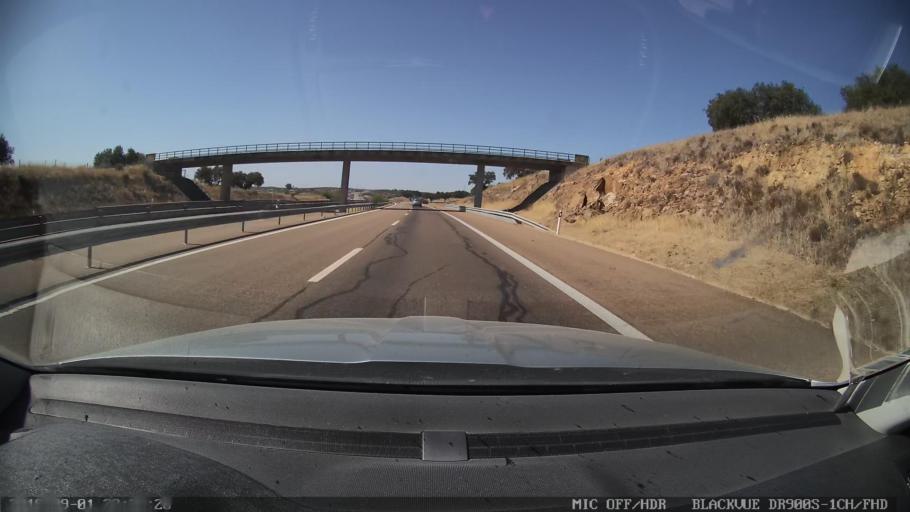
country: PT
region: Portalegre
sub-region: Elvas
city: Elvas
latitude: 38.8966
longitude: -7.2024
